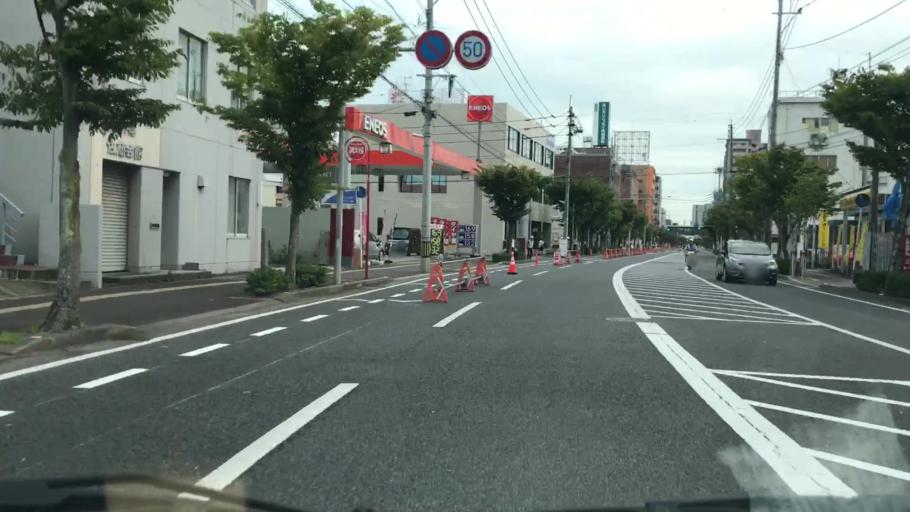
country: JP
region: Saga Prefecture
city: Saga-shi
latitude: 33.2691
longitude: 130.2963
